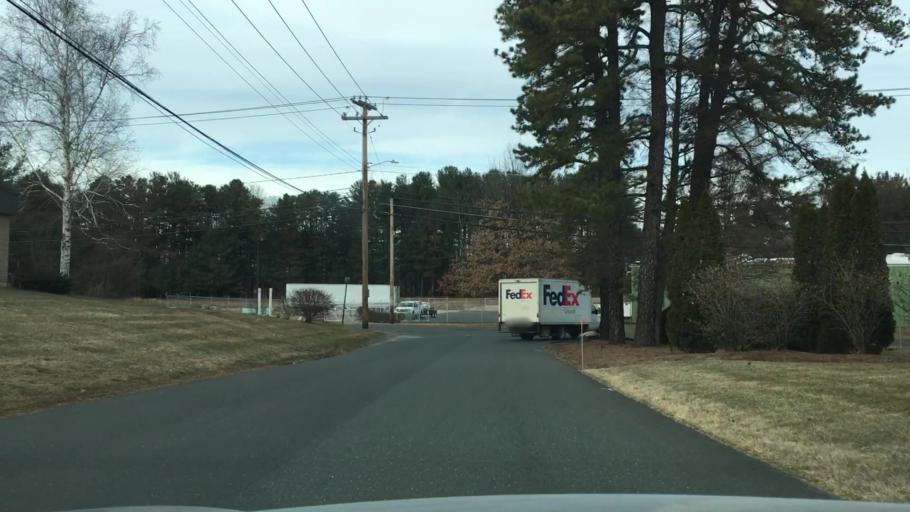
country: US
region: Massachusetts
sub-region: Hampden County
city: Westfield
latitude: 42.1532
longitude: -72.7458
